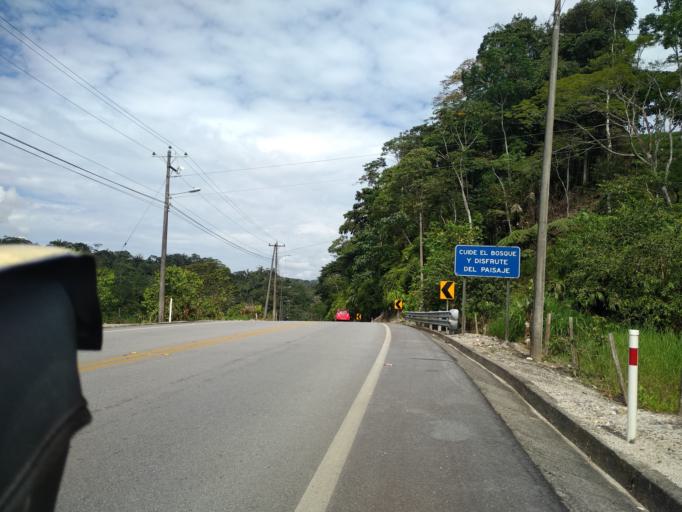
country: EC
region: Napo
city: Tena
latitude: -1.1207
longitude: -77.8160
